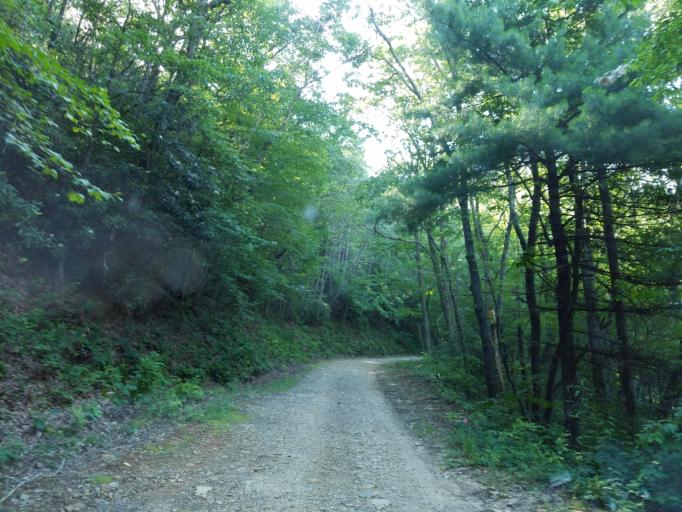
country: US
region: Georgia
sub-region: Dawson County
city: Dawsonville
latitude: 34.5968
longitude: -84.2107
